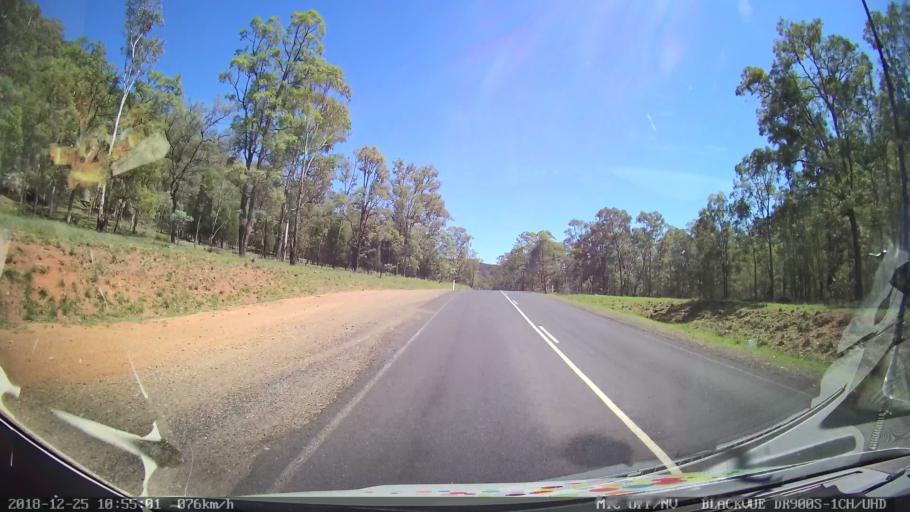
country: AU
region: New South Wales
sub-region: Upper Hunter Shire
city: Merriwa
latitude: -32.4034
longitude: 150.2730
